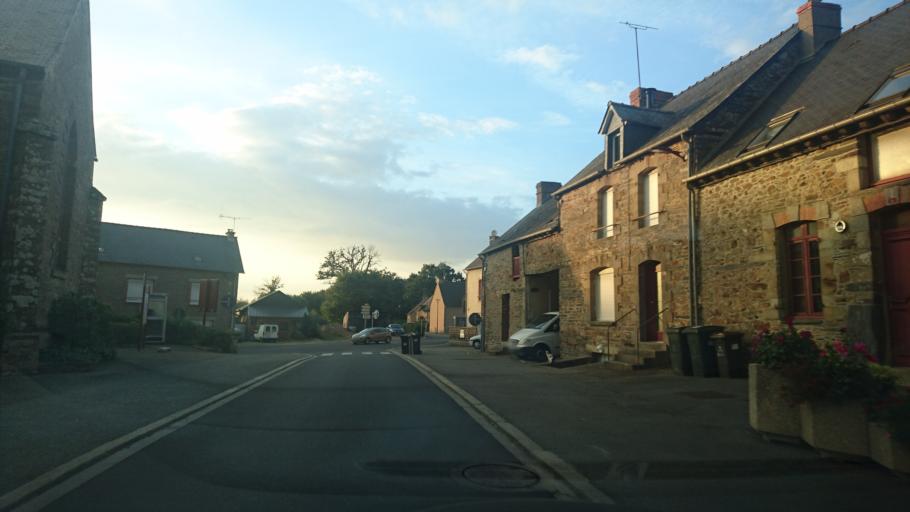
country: FR
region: Brittany
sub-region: Departement d'Ille-et-Vilaine
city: Pipriac
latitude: 47.8519
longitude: -1.9430
